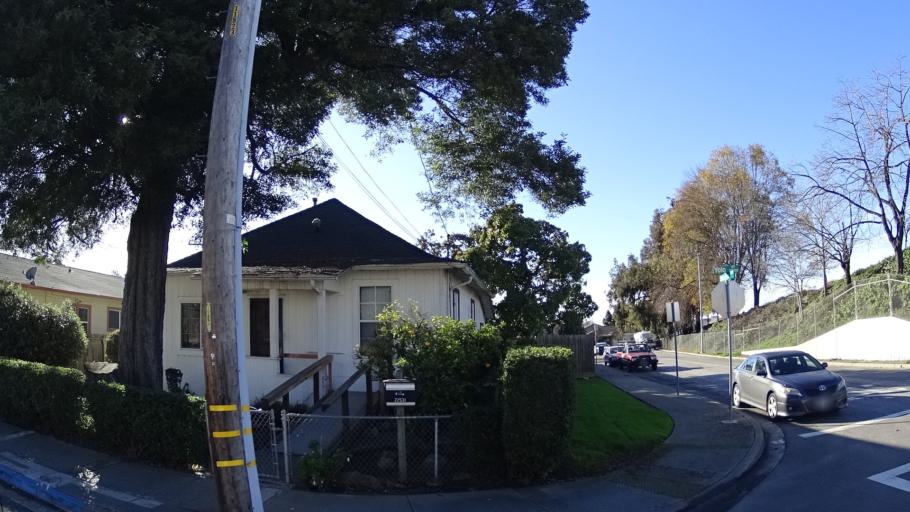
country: US
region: California
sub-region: Alameda County
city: Cherryland
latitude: 37.6660
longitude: -122.1012
